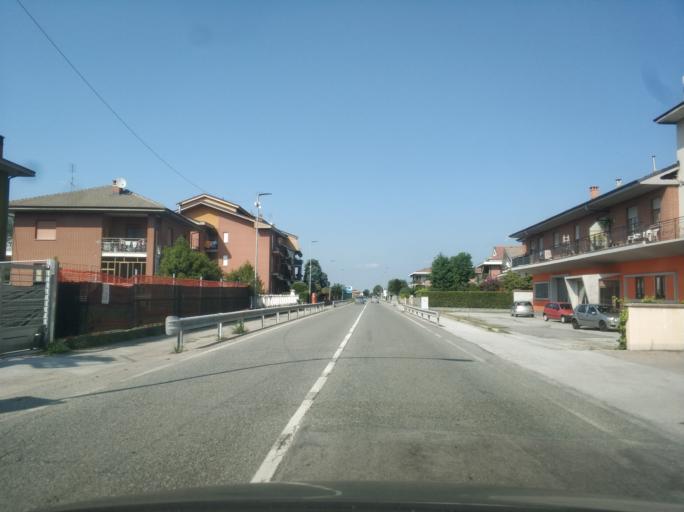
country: IT
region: Piedmont
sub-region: Provincia di Cuneo
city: Centallo
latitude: 44.5052
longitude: 7.5868
